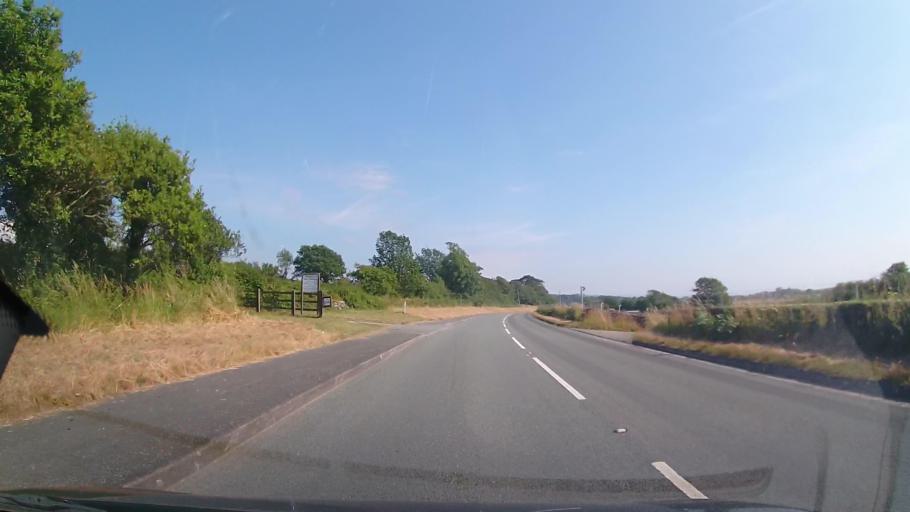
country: GB
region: Wales
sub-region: Gwynedd
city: Llanfair
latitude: 52.8340
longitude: -4.1128
